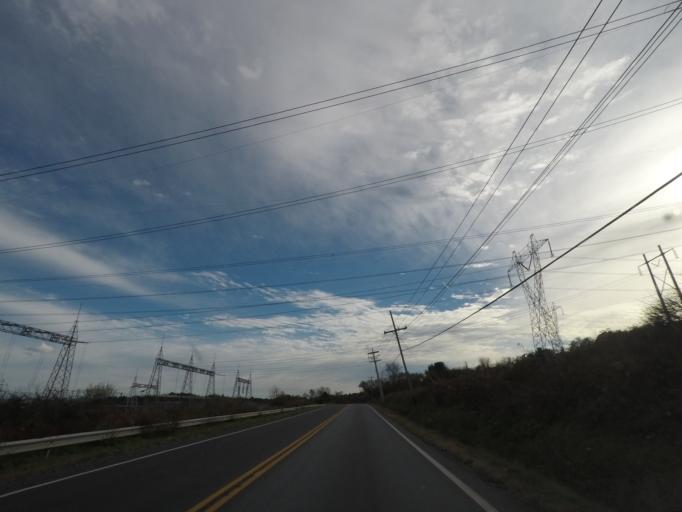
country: US
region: New York
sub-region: Albany County
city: Voorheesville
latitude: 42.6100
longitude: -73.9060
